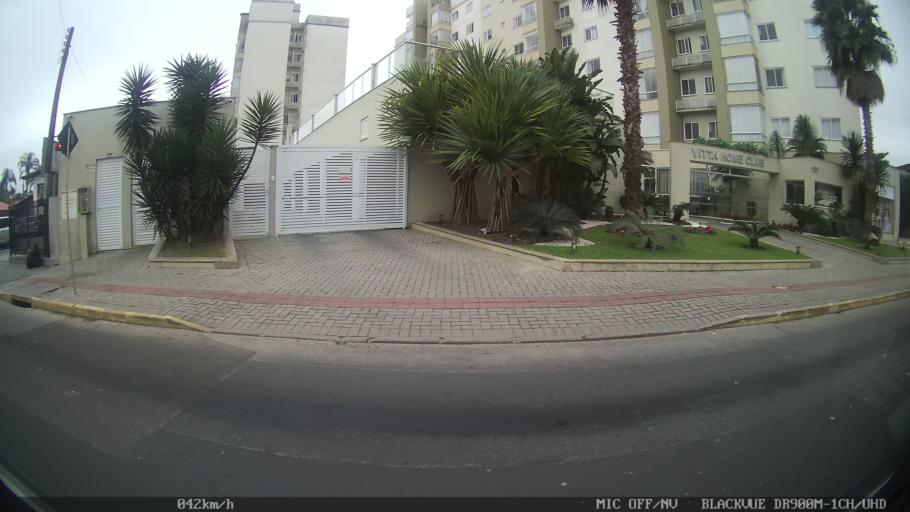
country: BR
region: Santa Catarina
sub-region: Joinville
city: Joinville
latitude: -26.2826
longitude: -48.8370
